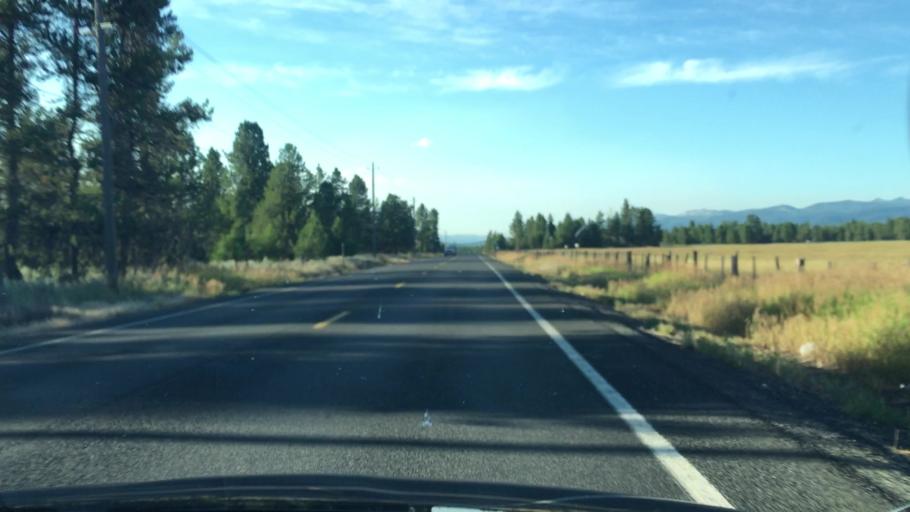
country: US
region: Idaho
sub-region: Valley County
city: McCall
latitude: 44.7820
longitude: -116.0768
